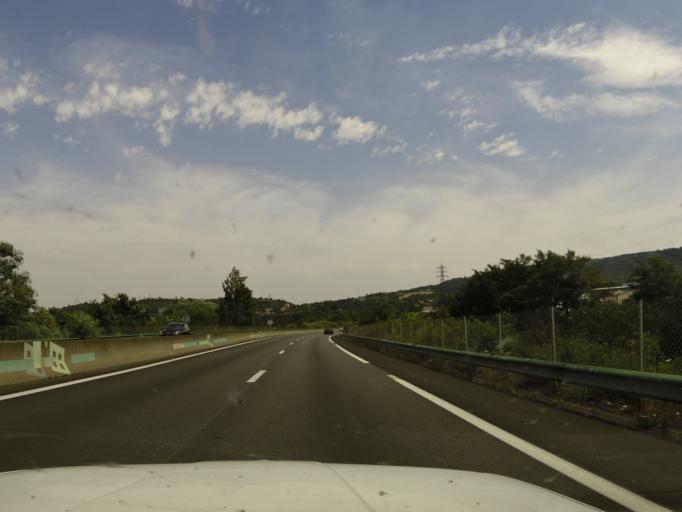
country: FR
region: Auvergne
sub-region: Departement du Puy-de-Dome
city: Beaumont
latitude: 45.7468
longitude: 3.0962
